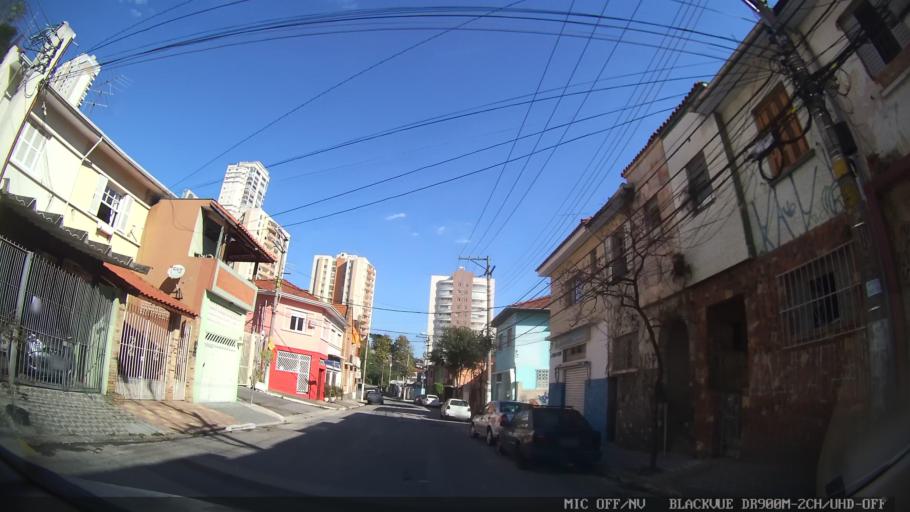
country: BR
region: Sao Paulo
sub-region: Sao Paulo
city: Sao Paulo
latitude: -23.4961
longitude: -46.6324
